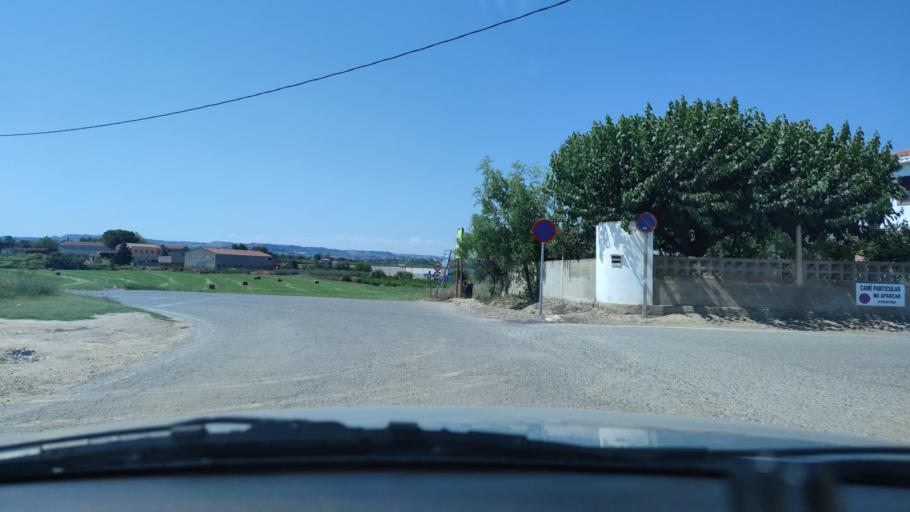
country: ES
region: Catalonia
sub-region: Provincia de Lleida
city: Lleida
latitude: 41.6427
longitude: 0.6240
